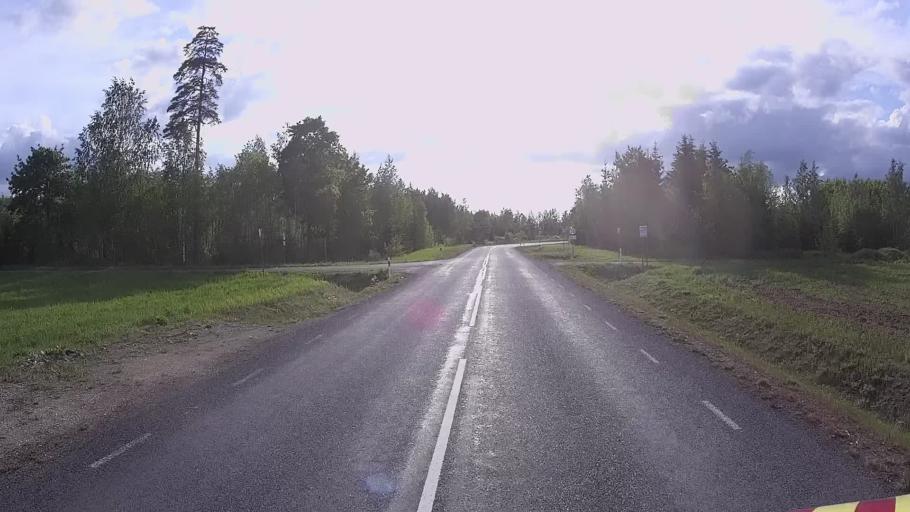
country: EE
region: Jogevamaa
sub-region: Mustvee linn
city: Mustvee
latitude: 59.0481
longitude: 27.0342
